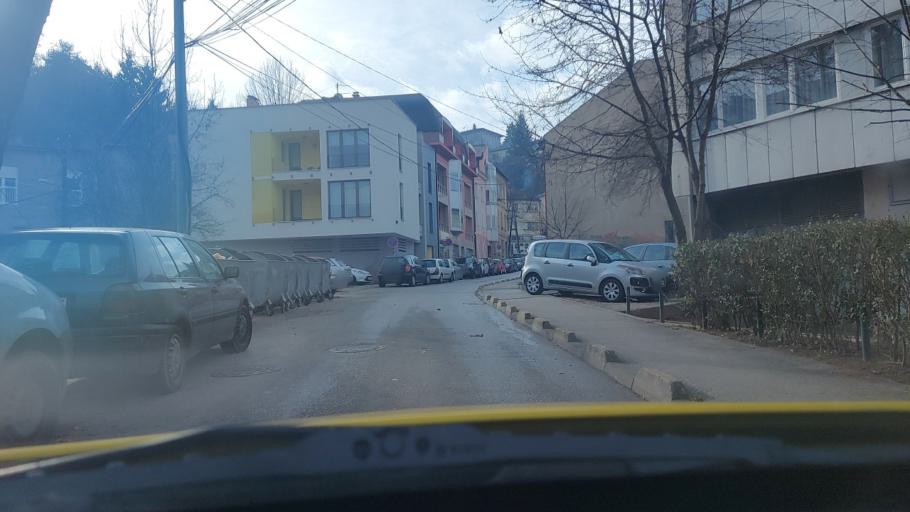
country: BA
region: Federation of Bosnia and Herzegovina
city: Kobilja Glava
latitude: 43.8545
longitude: 18.4178
